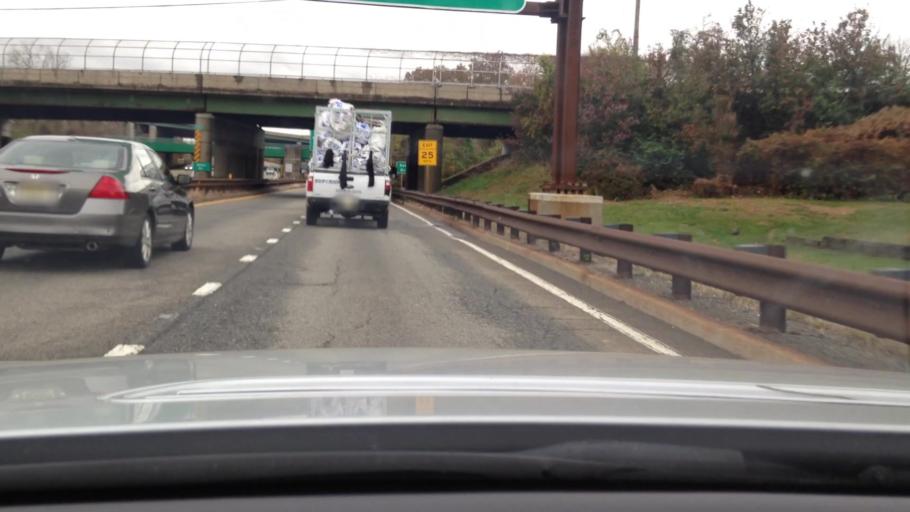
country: US
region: New Jersey
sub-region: Bergen County
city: Elmwood Park
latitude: 40.9058
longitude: -74.1049
